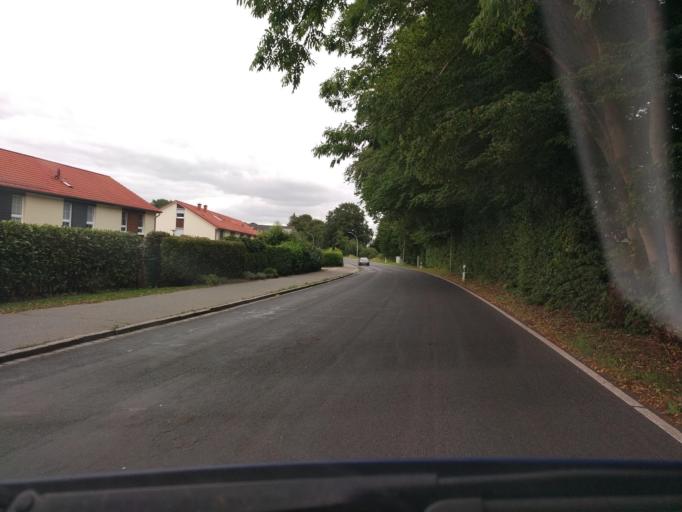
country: DE
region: Schleswig-Holstein
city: Neuberend
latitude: 54.5240
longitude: 9.5280
